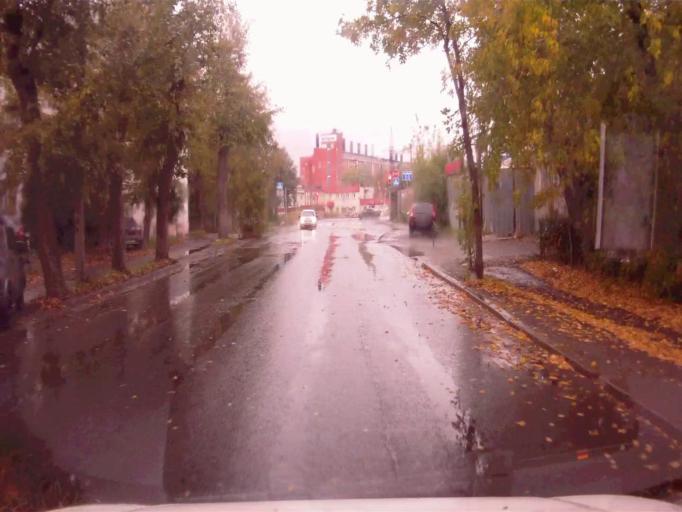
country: RU
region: Chelyabinsk
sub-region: Gorod Chelyabinsk
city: Chelyabinsk
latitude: 55.1980
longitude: 61.4071
